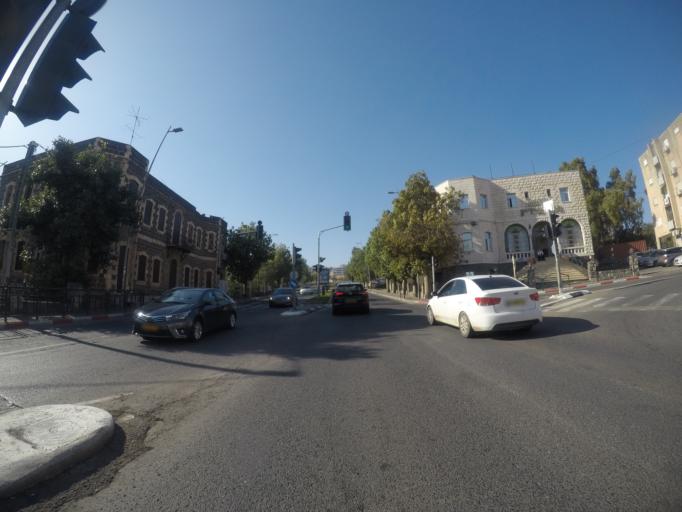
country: IL
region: Northern District
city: Tiberias
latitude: 32.7931
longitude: 35.5341
